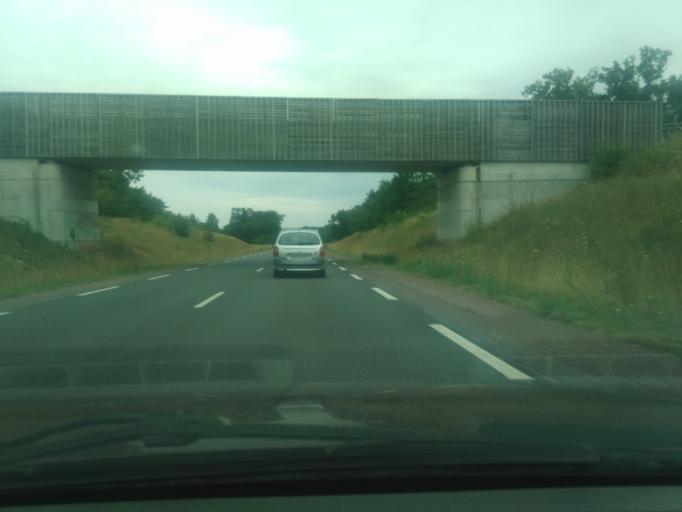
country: FR
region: Poitou-Charentes
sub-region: Departement de la Vienne
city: Saint-Savin
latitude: 46.5915
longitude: 0.9562
